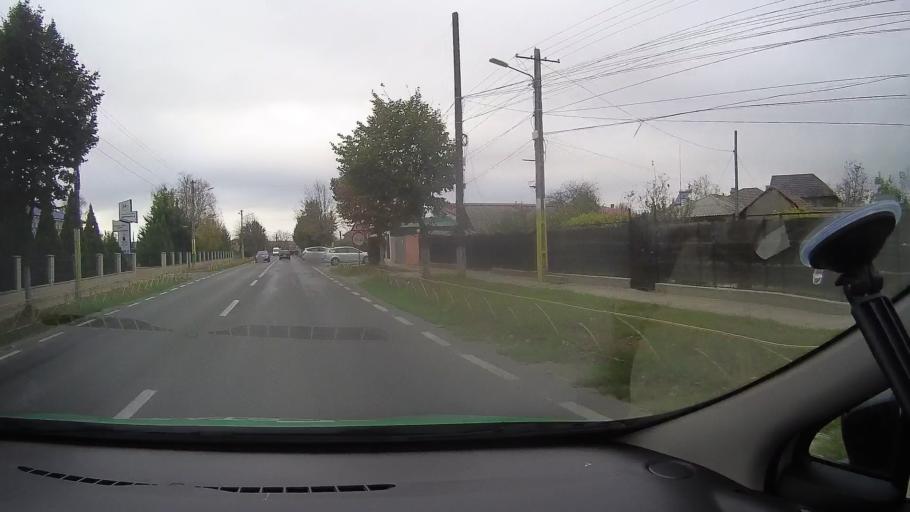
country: RO
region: Constanta
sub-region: Oras Murfatlar
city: Murfatlar
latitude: 44.1755
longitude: 28.4068
